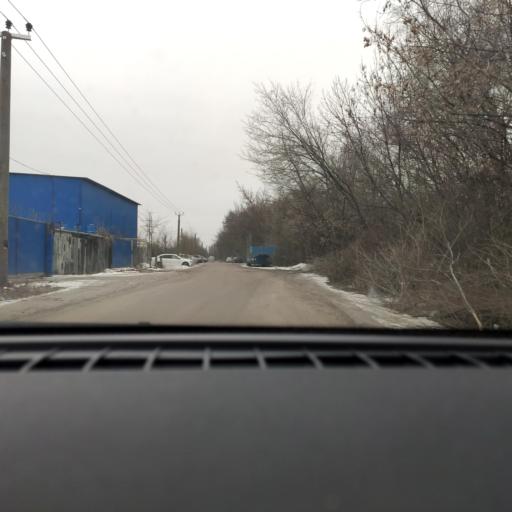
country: RU
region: Voronezj
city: Voronezh
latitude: 51.6511
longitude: 39.2654
